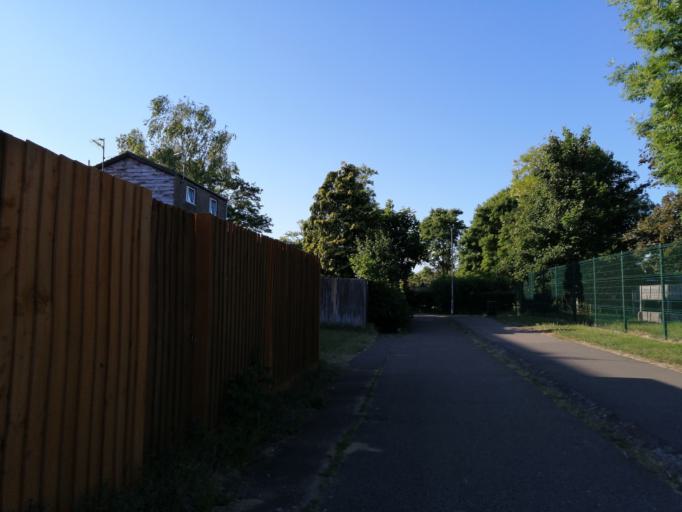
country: GB
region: England
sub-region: Peterborough
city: Marholm
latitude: 52.6001
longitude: -0.2829
